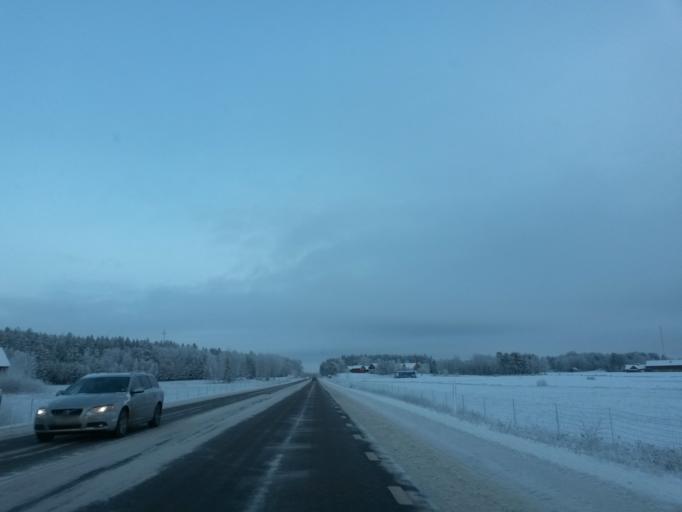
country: SE
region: Vaestra Goetaland
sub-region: Vara Kommun
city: Vara
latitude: 58.1569
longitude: 12.8749
